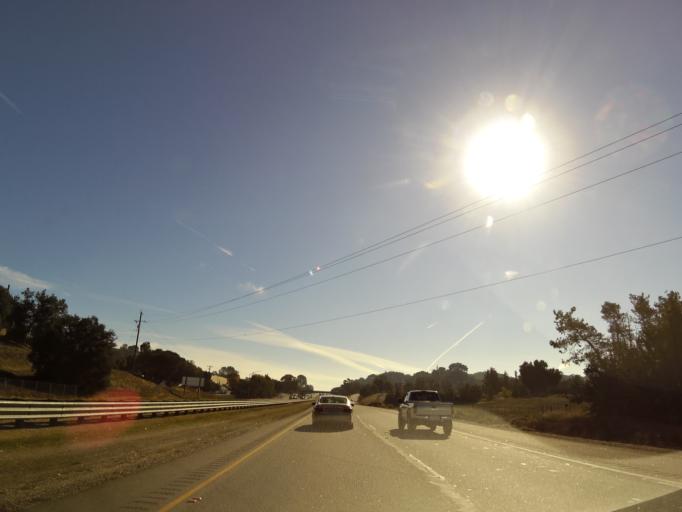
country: US
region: California
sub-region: San Luis Obispo County
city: Atascadero
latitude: 35.5002
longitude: -120.6876
